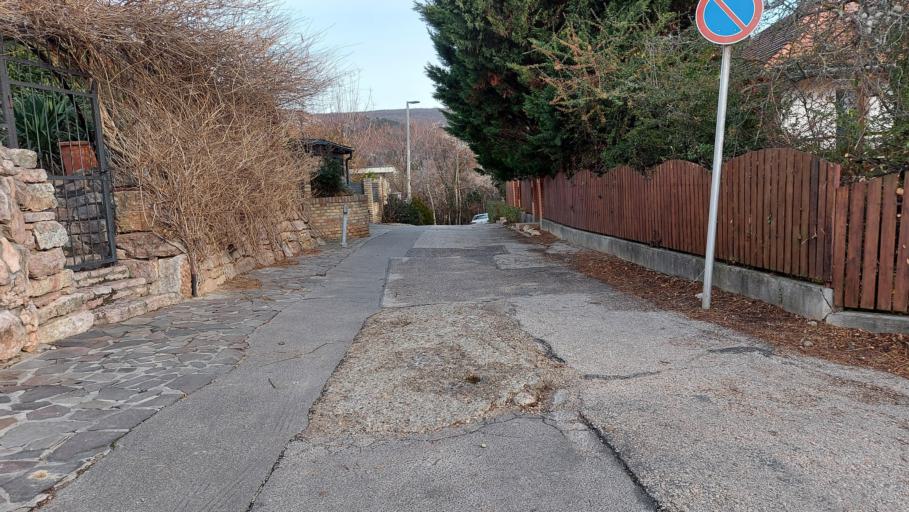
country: HU
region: Pest
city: Budaors
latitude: 47.4642
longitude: 18.9364
